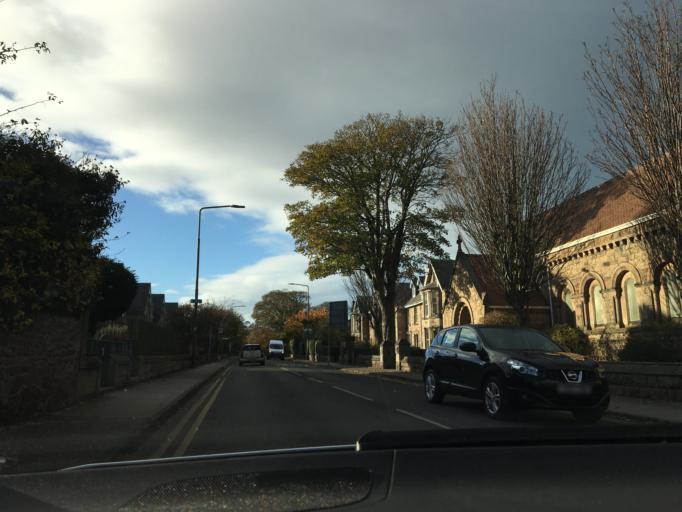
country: GB
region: Scotland
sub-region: East Lothian
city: North Berwick
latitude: 56.0583
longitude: -2.7303
